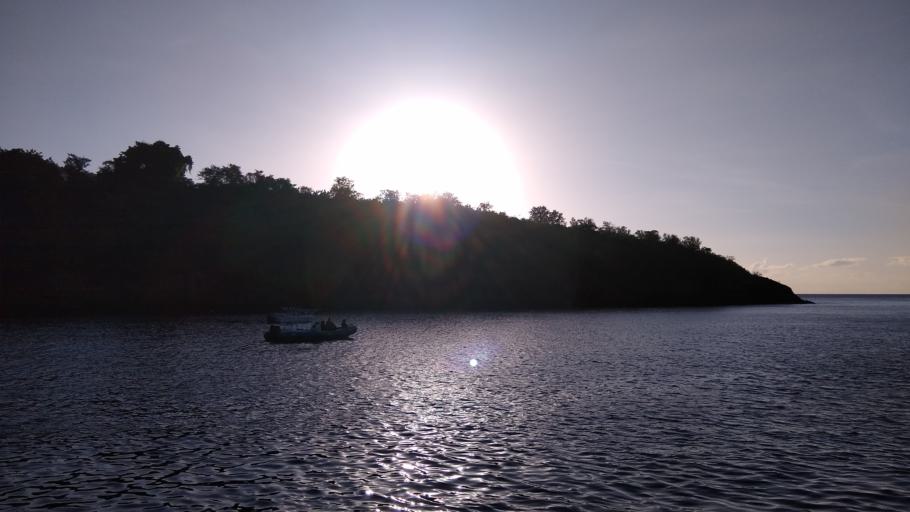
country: MQ
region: Martinique
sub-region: Martinique
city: Les Trois-Ilets
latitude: 14.5282
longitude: -61.0878
